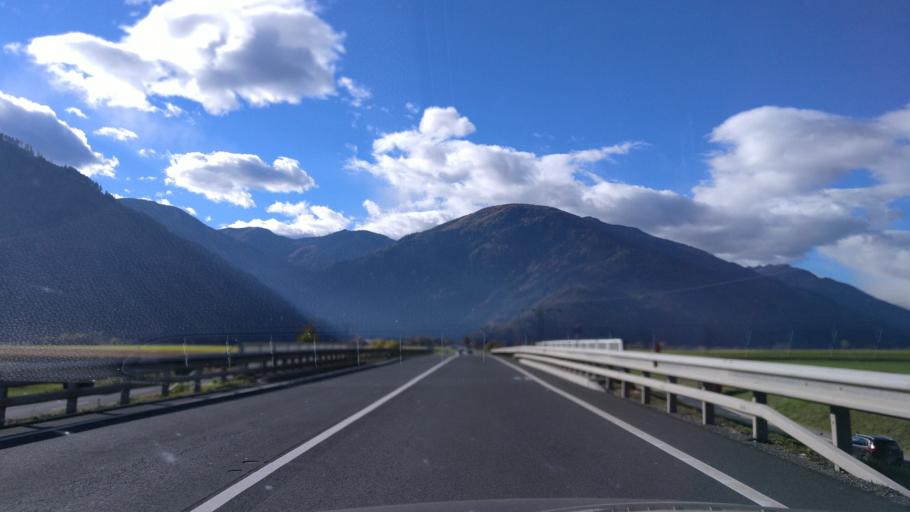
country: AT
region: Carinthia
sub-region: Politischer Bezirk Spittal an der Drau
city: Lendorf
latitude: 46.8328
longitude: 13.4019
